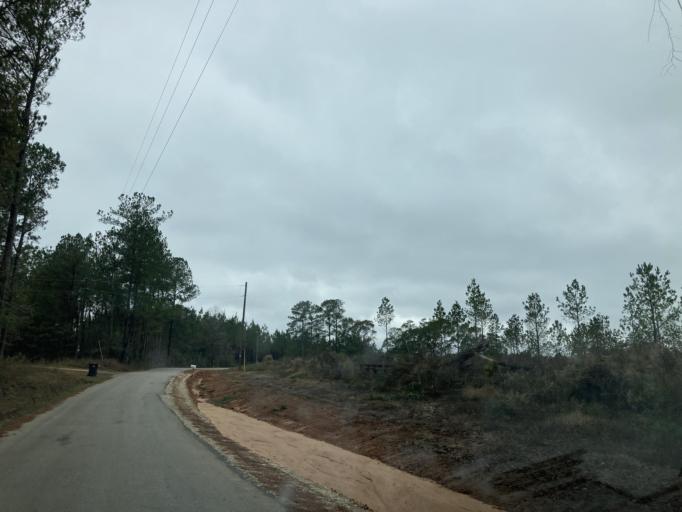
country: US
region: Mississippi
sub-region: Lamar County
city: Purvis
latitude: 31.1857
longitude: -89.4252
